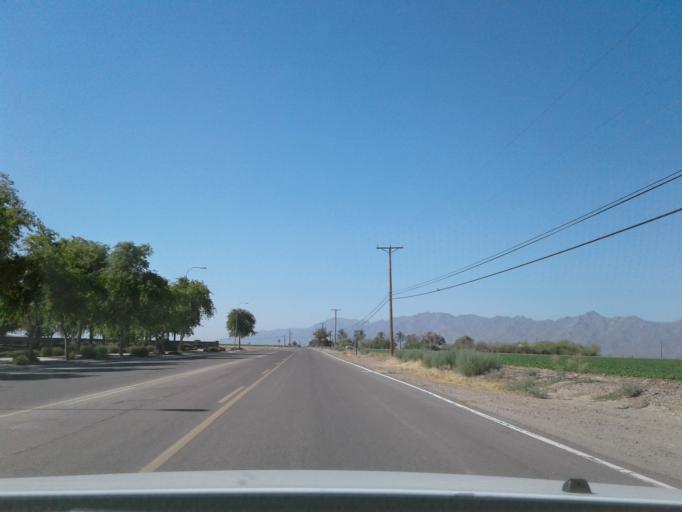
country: US
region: Arizona
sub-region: Maricopa County
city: Laveen
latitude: 33.3660
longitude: -112.1863
